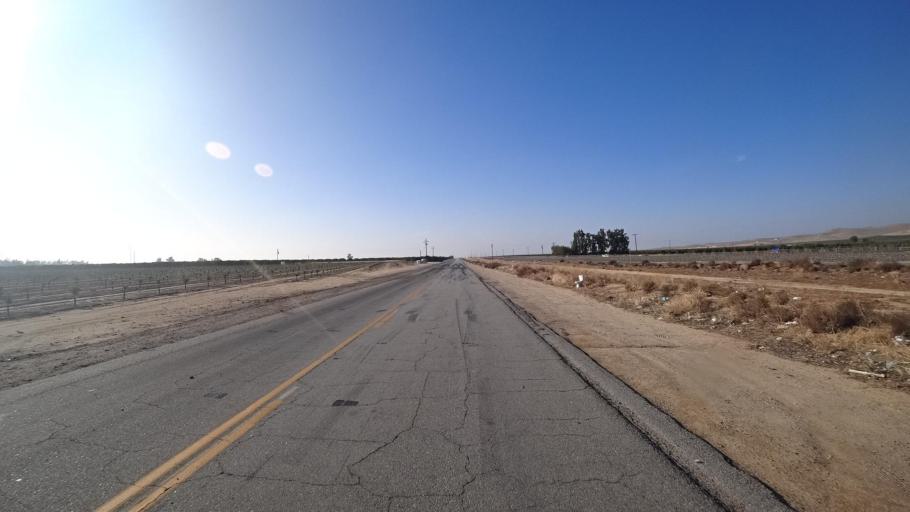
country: US
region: California
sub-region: Kern County
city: Arvin
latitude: 35.3254
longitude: -118.7780
